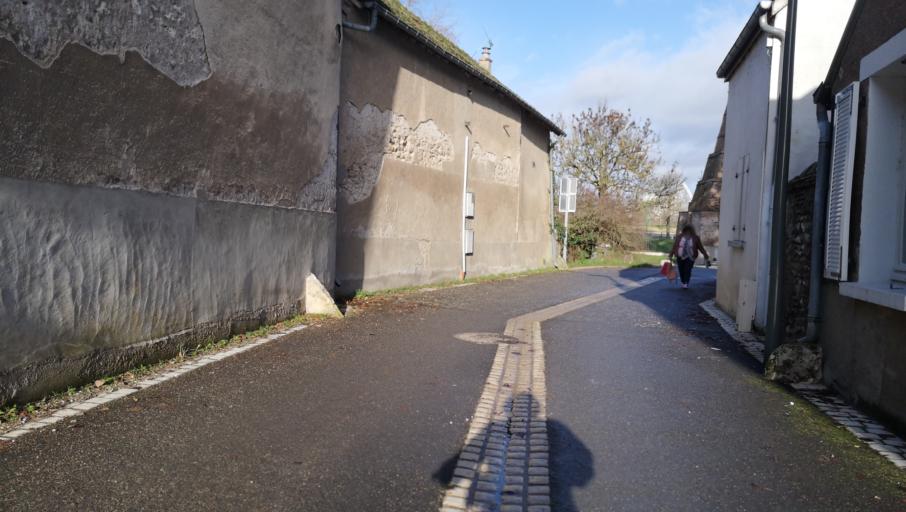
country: FR
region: Centre
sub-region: Departement du Loiret
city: Saint-Pryve-Saint-Mesmin
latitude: 47.8917
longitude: 1.8755
